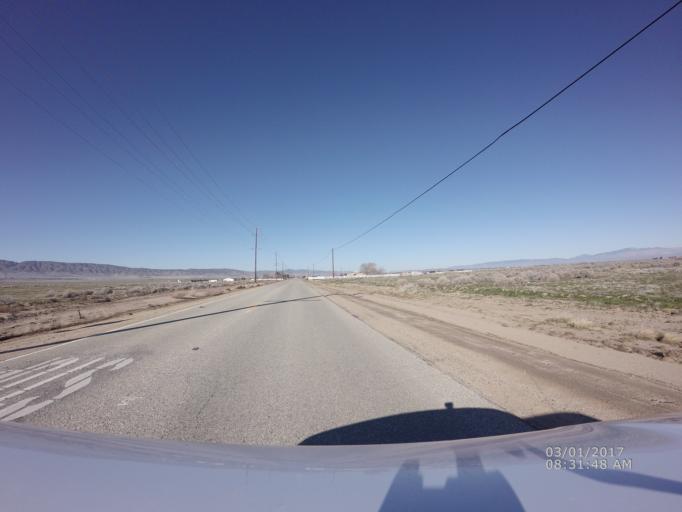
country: US
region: California
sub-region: Los Angeles County
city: Quartz Hill
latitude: 34.6894
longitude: -118.2562
